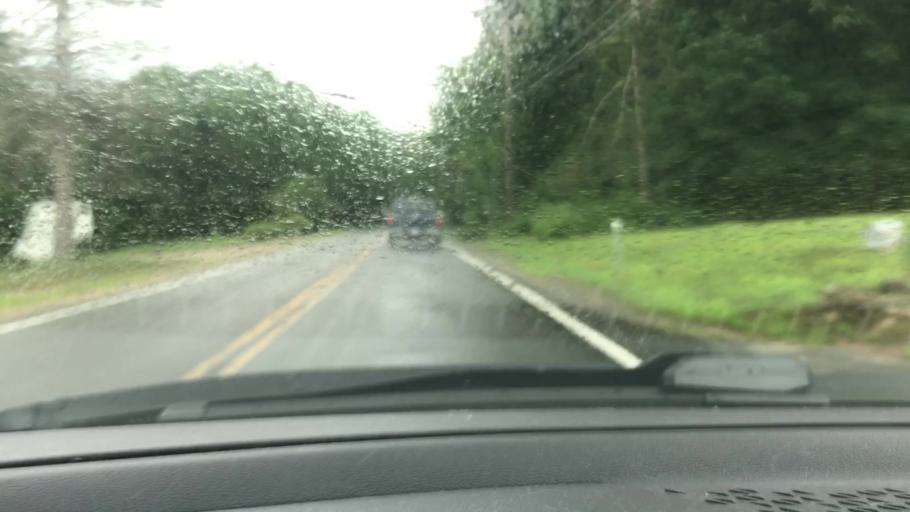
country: US
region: New Hampshire
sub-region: Merrimack County
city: Epsom
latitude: 43.1893
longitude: -71.2686
